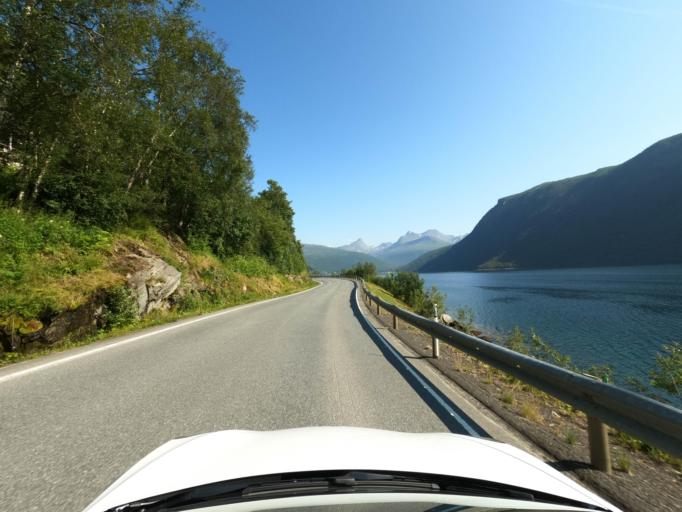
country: NO
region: Nordland
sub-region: Narvik
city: Narvik
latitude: 68.3973
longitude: 17.5068
